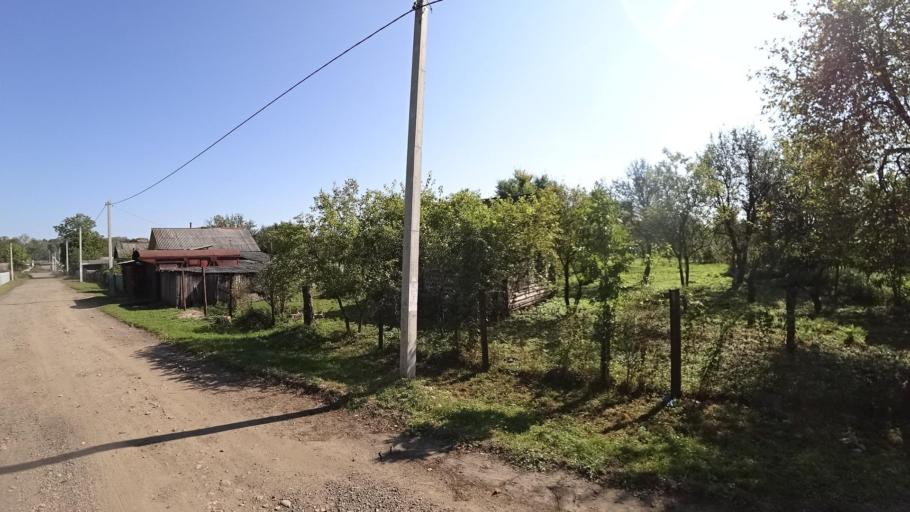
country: RU
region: Jewish Autonomous Oblast
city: Bira
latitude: 48.9953
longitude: 132.4659
